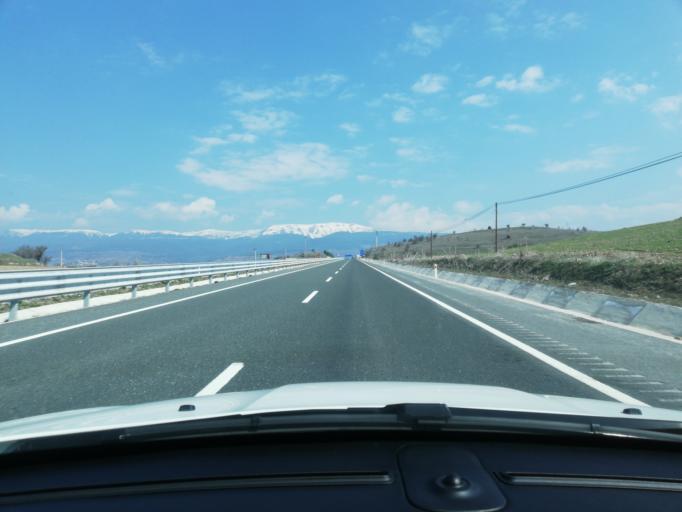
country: TR
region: Cankiri
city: Ilgaz
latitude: 40.9136
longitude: 33.6492
